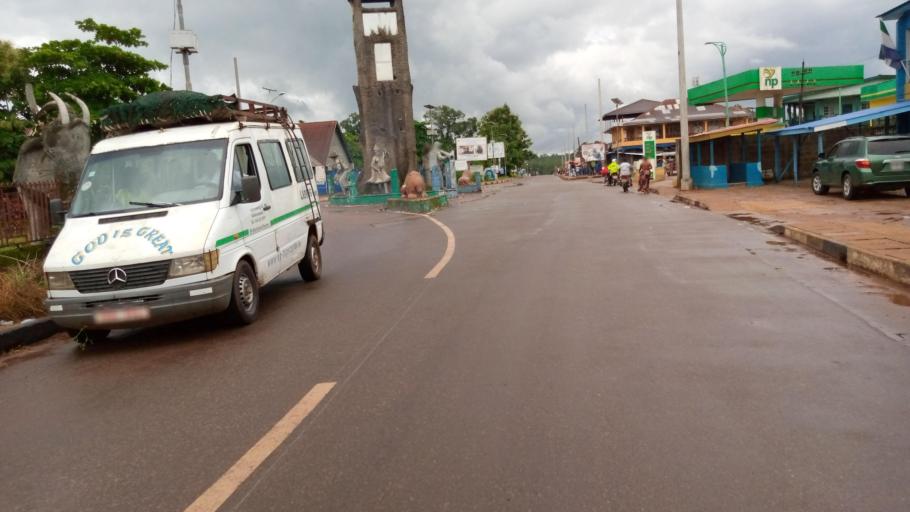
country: SL
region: Southern Province
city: Moyamba
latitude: 8.1601
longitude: -12.4335
